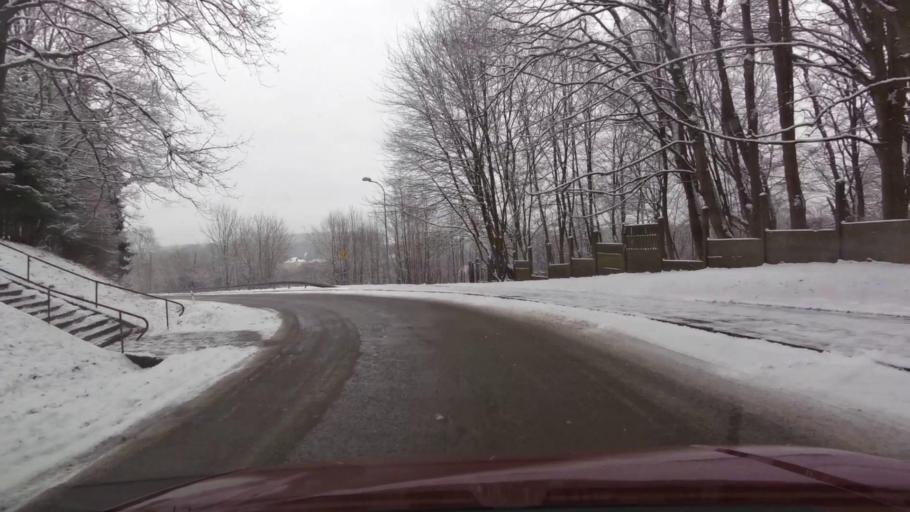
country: PL
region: West Pomeranian Voivodeship
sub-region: Powiat swidwinski
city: Rabino
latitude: 53.8676
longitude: 15.9460
